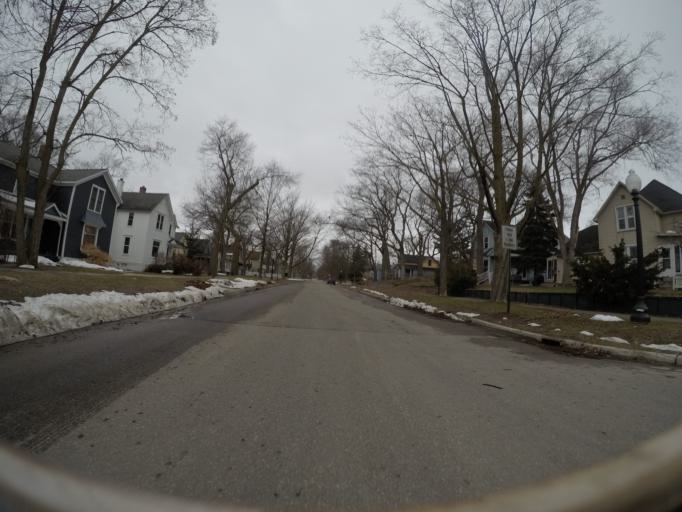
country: US
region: Michigan
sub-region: Grand Traverse County
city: Traverse City
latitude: 44.7606
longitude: -85.6089
